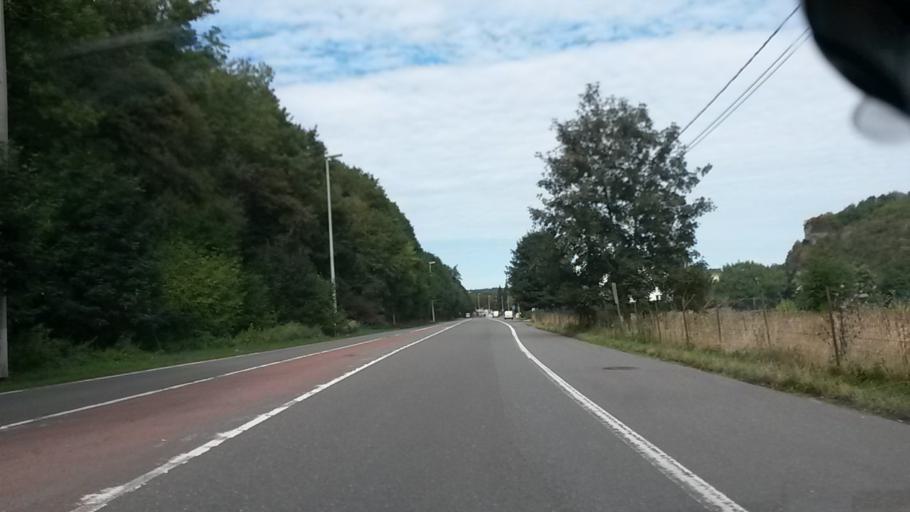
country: BE
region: Wallonia
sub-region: Province de Namur
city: Noville-les-Bois
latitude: 50.4677
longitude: 4.9893
